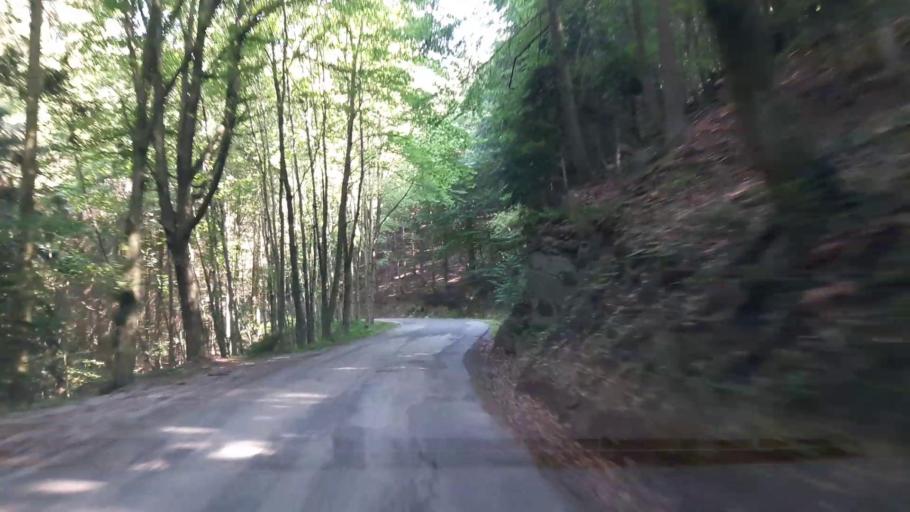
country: AT
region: Lower Austria
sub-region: Politischer Bezirk Krems
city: Aggsbach
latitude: 48.2917
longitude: 15.3686
